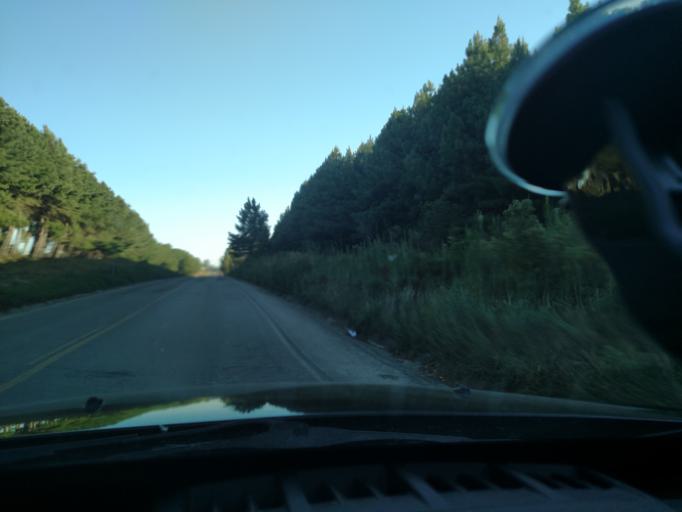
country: BR
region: Santa Catarina
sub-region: Lages
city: Lages
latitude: -27.7236
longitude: -50.2031
